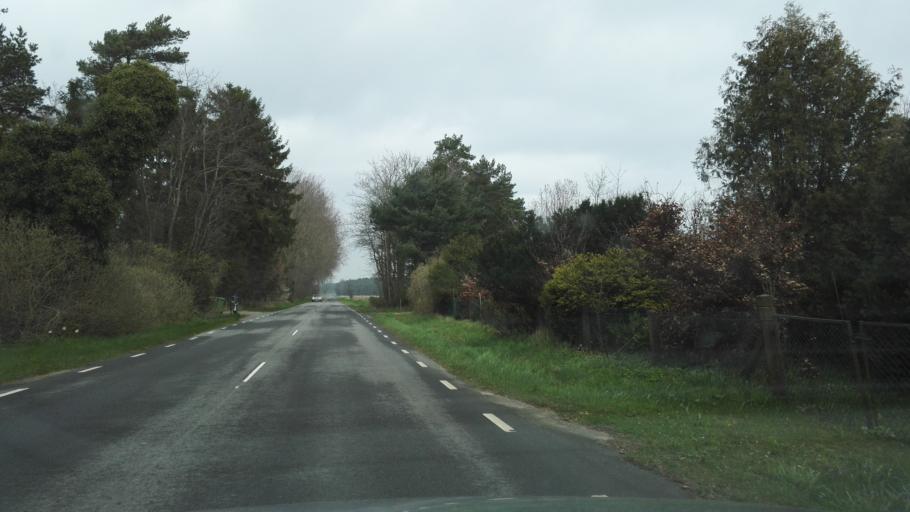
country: SE
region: Skane
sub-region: Simrishamns Kommun
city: Simrishamn
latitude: 55.4243
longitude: 14.2162
